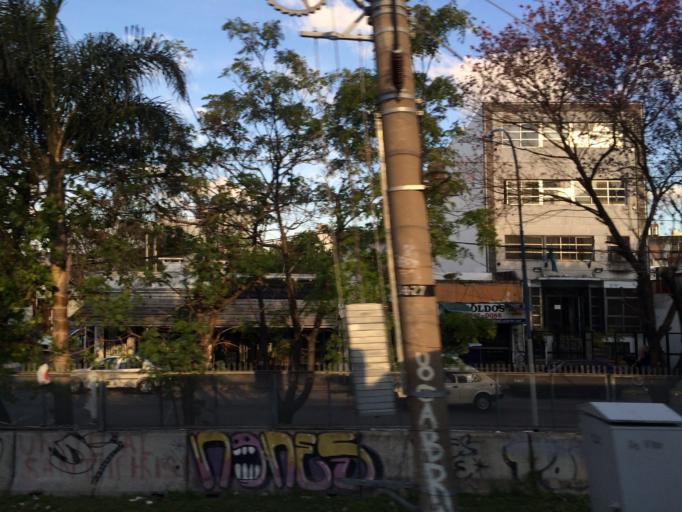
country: AR
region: Buenos Aires
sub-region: Partido de Lanus
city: Lanus
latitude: -34.7048
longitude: -58.3895
